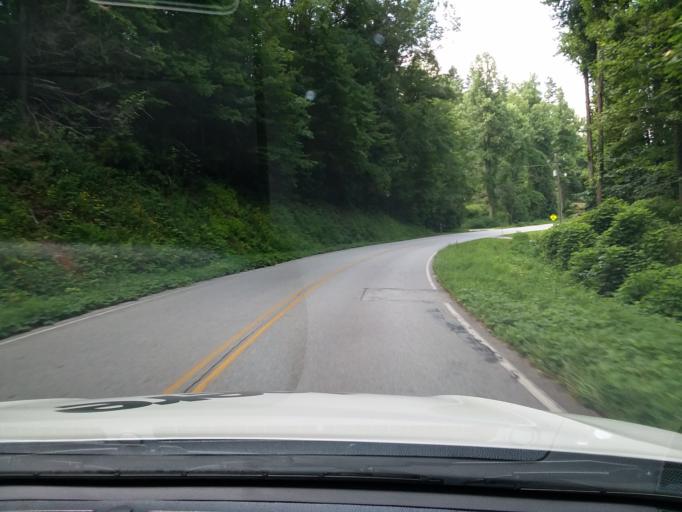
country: US
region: Georgia
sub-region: Rabun County
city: Clayton
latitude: 34.7612
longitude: -83.3995
